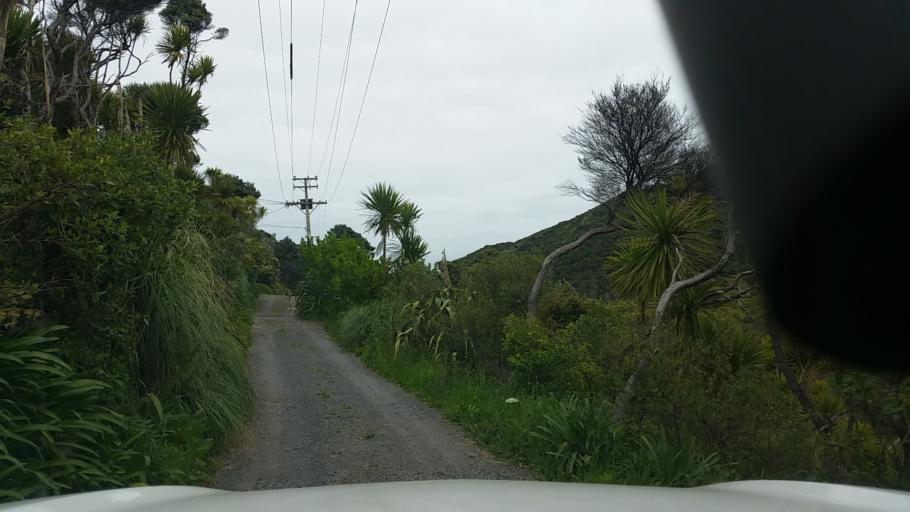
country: NZ
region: Auckland
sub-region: Auckland
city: Muriwai Beach
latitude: -36.8800
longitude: 174.4516
